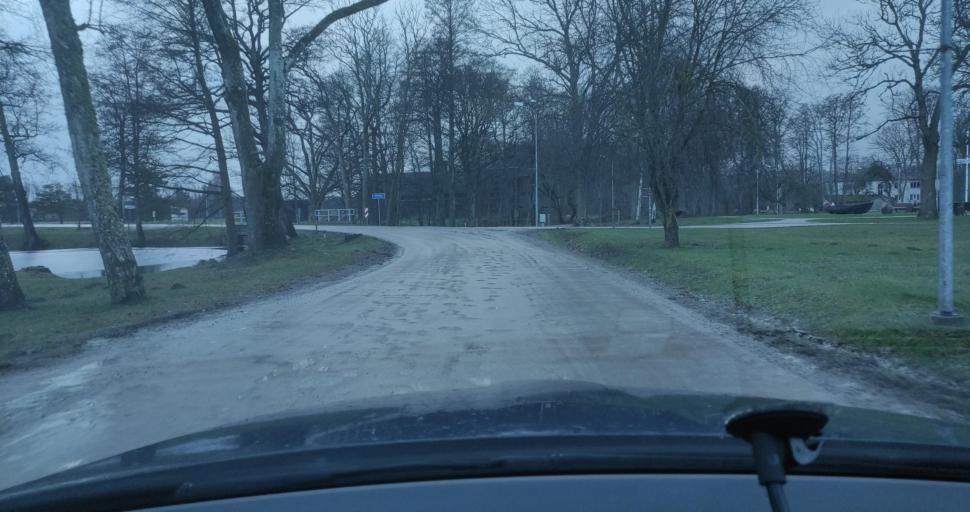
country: LV
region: Pavilostas
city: Pavilosta
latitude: 56.7486
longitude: 21.0777
